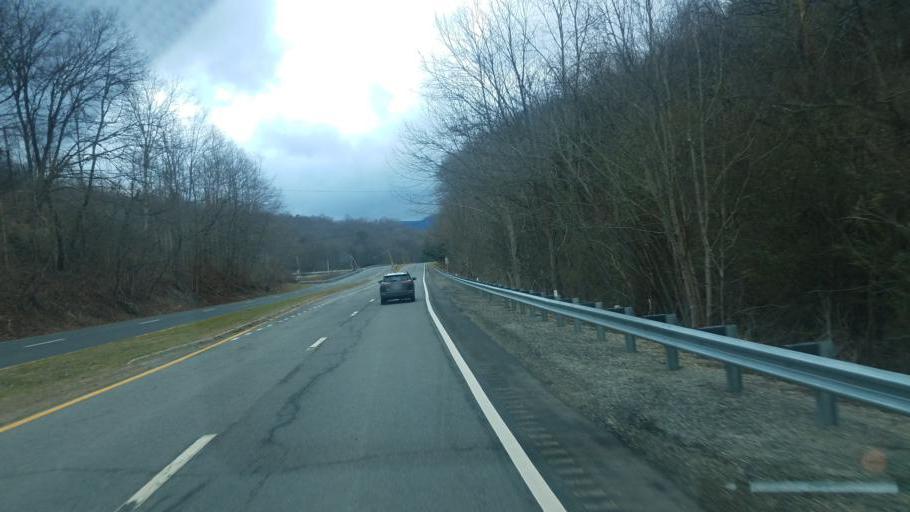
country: US
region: Virginia
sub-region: Giles County
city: Pearisburg
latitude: 37.2701
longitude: -80.7274
